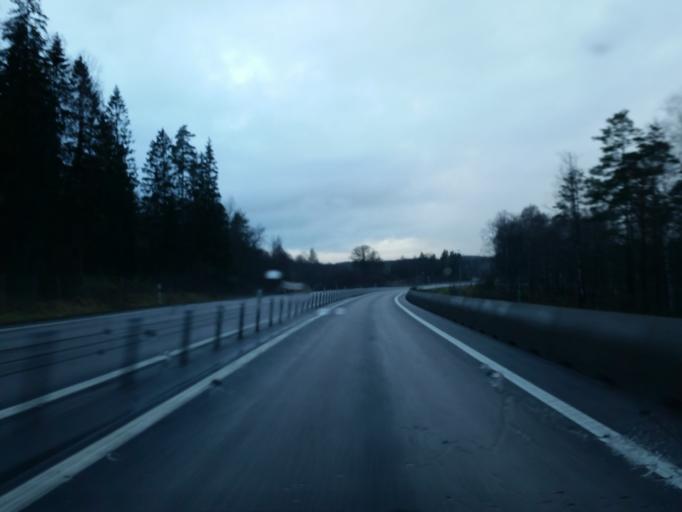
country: SE
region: Vaestra Goetaland
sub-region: Boras Kommun
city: Ganghester
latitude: 57.6768
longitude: 12.9776
